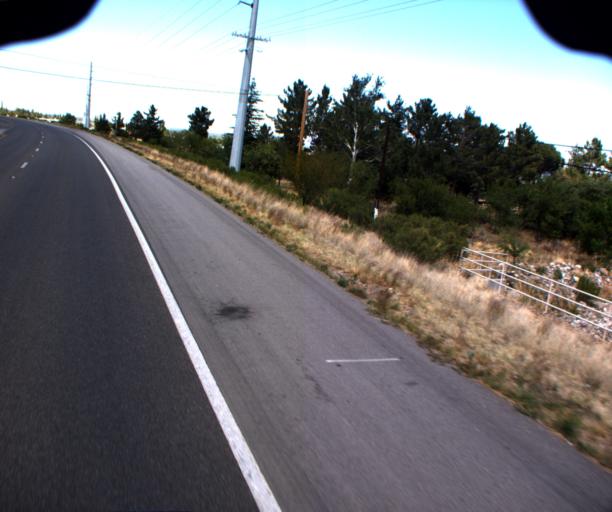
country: US
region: Arizona
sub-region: Cochise County
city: Sierra Vista Southeast
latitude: 31.4283
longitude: -110.2407
